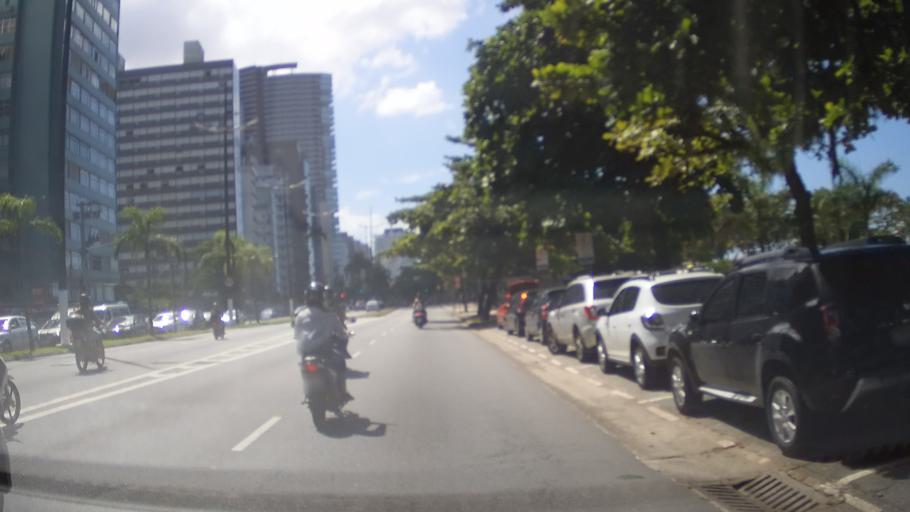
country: BR
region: Sao Paulo
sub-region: Santos
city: Santos
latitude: -23.9680
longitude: -46.3470
